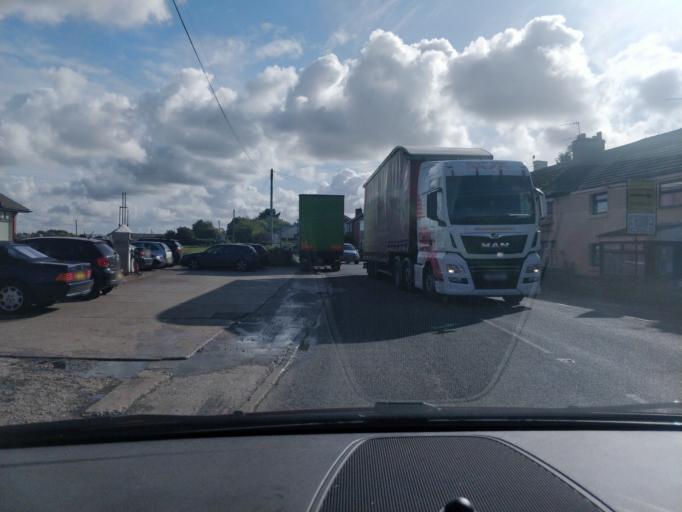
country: GB
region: England
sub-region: Lancashire
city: Ormskirk
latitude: 53.5995
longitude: -2.9017
